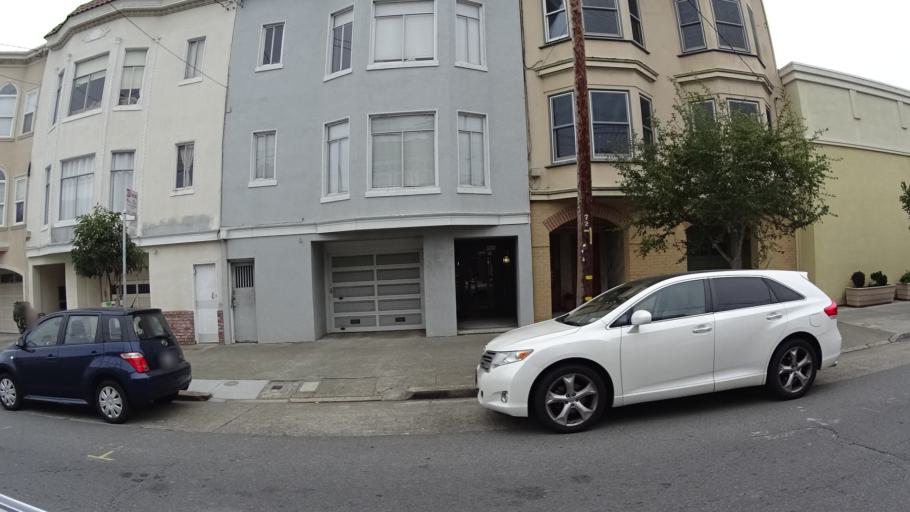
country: US
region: California
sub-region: San Francisco County
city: San Francisco
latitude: 37.7747
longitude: -122.4660
